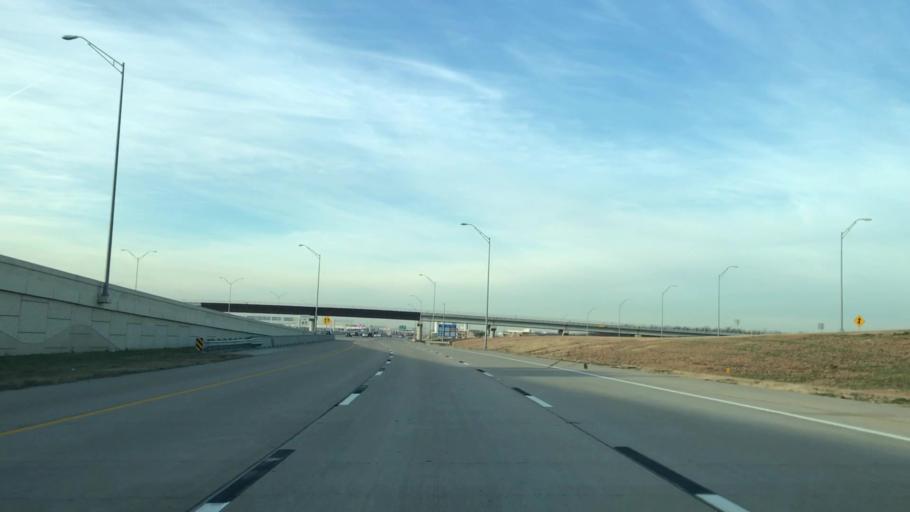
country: US
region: Texas
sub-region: Tarrant County
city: Grapevine
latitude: 32.9312
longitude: -97.0473
